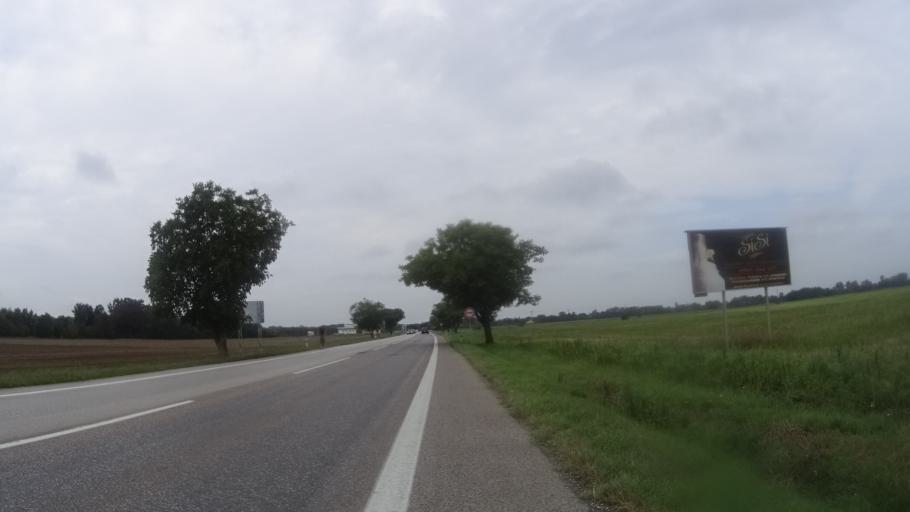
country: SK
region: Nitriansky
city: Komarno
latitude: 47.7649
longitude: 18.0745
